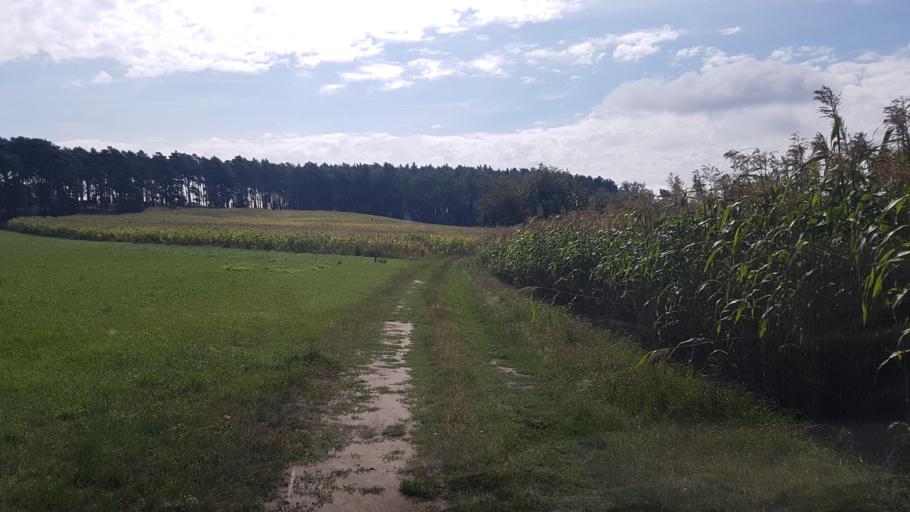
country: DE
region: Brandenburg
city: Hohenbucko
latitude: 51.7233
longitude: 13.4843
